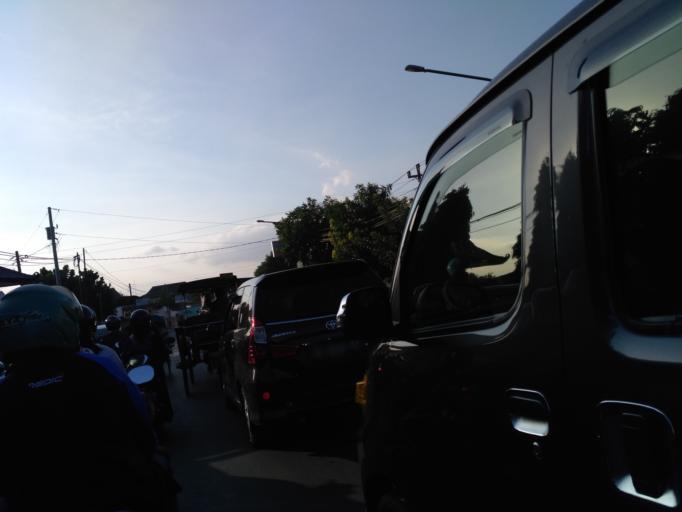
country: ID
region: Daerah Istimewa Yogyakarta
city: Sewon
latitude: -7.8335
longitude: 110.3904
